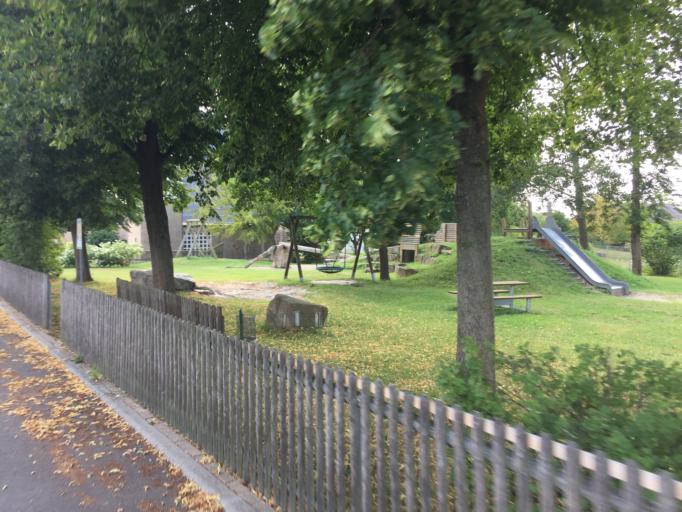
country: DE
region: Hesse
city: Schwalmstadt
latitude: 50.9045
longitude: 9.2733
